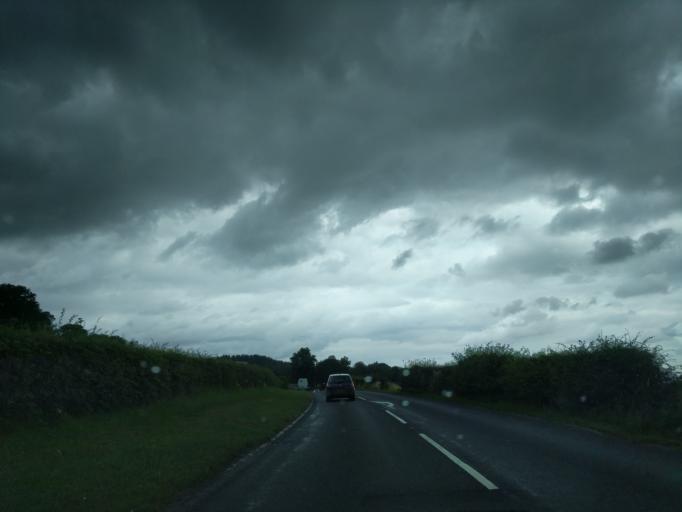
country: GB
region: England
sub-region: Staffordshire
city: Colwich
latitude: 52.7822
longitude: -1.9821
